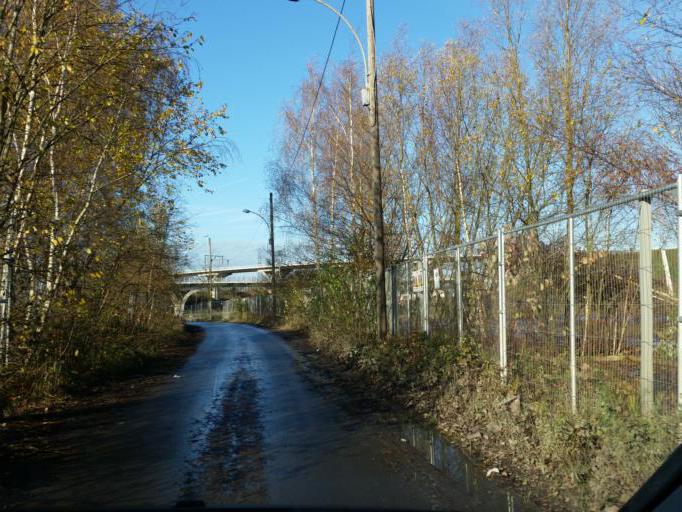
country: BE
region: Flanders
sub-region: Provincie Vlaams-Brabant
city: Diegem
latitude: 50.8980
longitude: 4.4266
